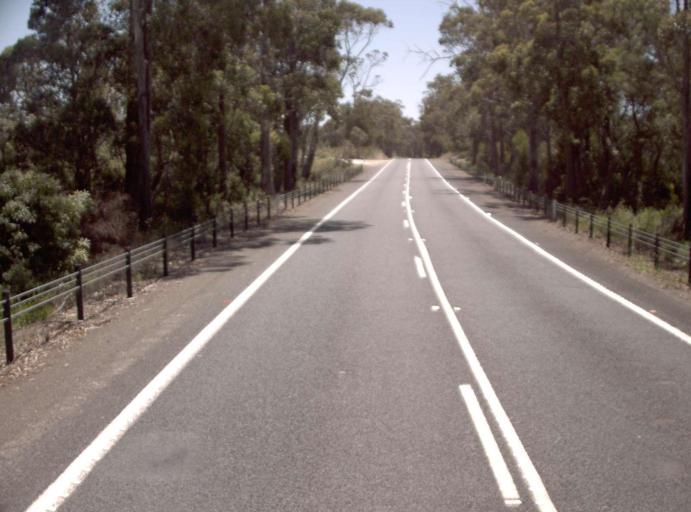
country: AU
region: Victoria
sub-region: East Gippsland
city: Lakes Entrance
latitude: -37.8368
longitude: 148.0322
